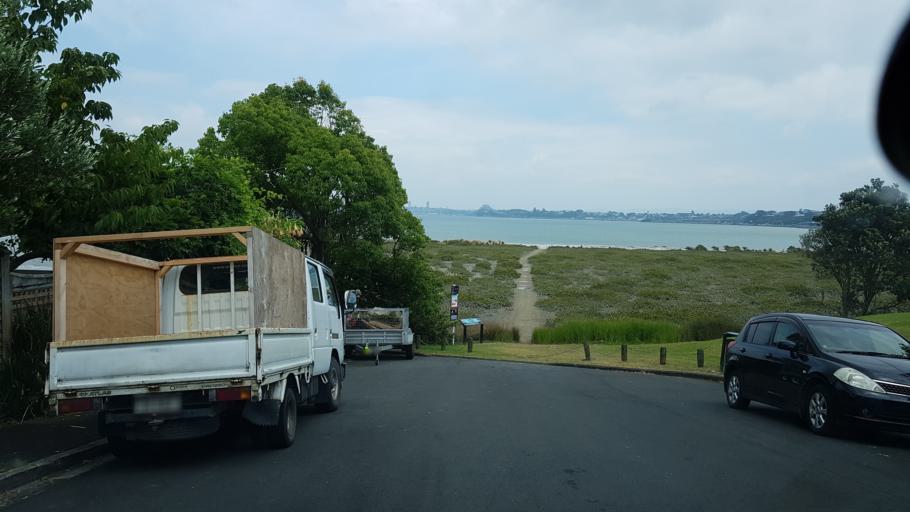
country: NZ
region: Auckland
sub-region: Auckland
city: North Shore
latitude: -36.8016
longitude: 174.7700
